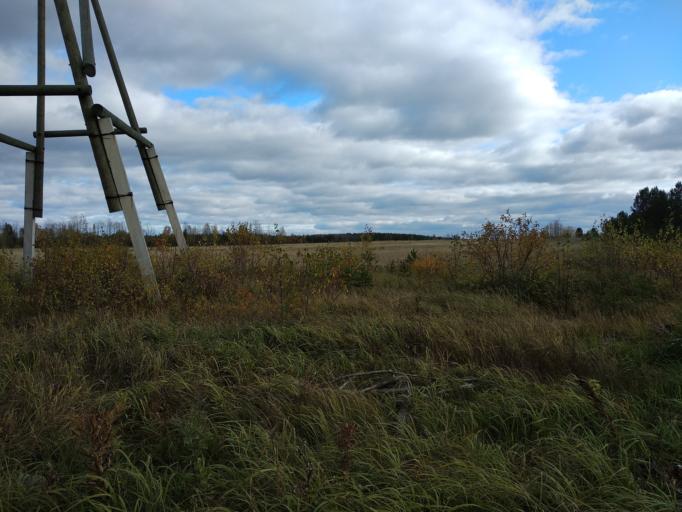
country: RU
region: Sverdlovsk
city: Krasnotur'insk
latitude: 59.8665
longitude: 60.2836
